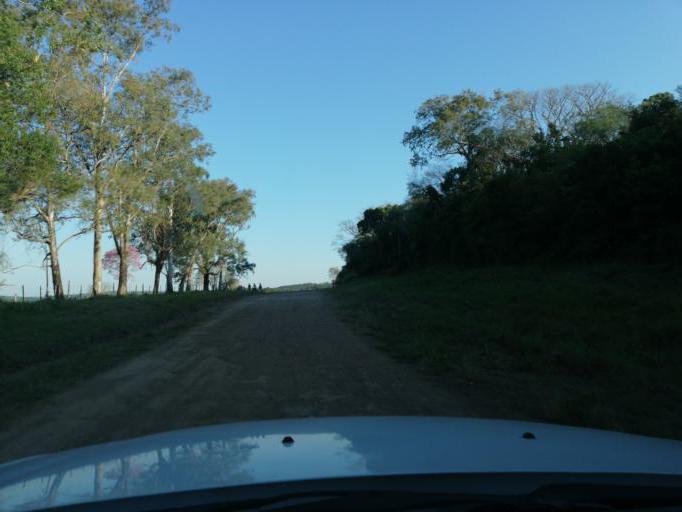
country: AR
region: Misiones
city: Cerro Cora
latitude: -27.6251
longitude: -55.7039
